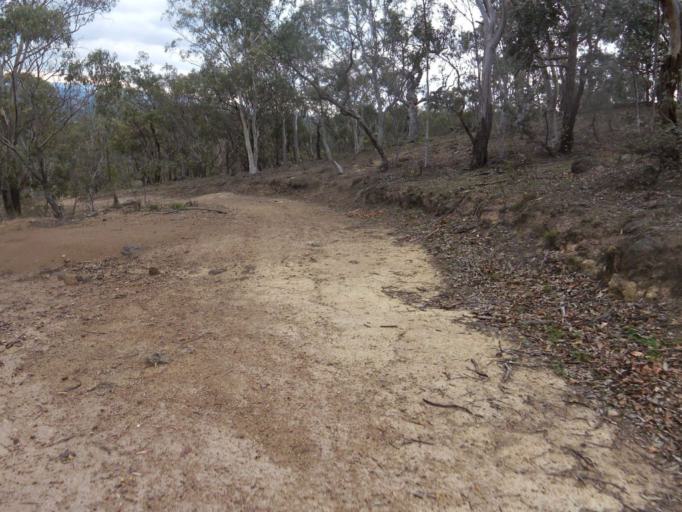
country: AU
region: Australian Capital Territory
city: Forrest
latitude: -35.3510
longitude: 149.1237
